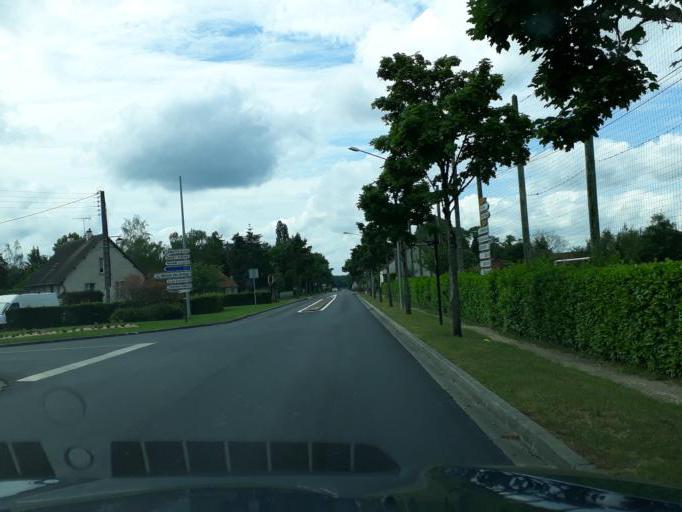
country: FR
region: Centre
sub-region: Departement du Loir-et-Cher
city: Chaumont-sur-Tharonne
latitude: 47.6076
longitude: 1.9029
